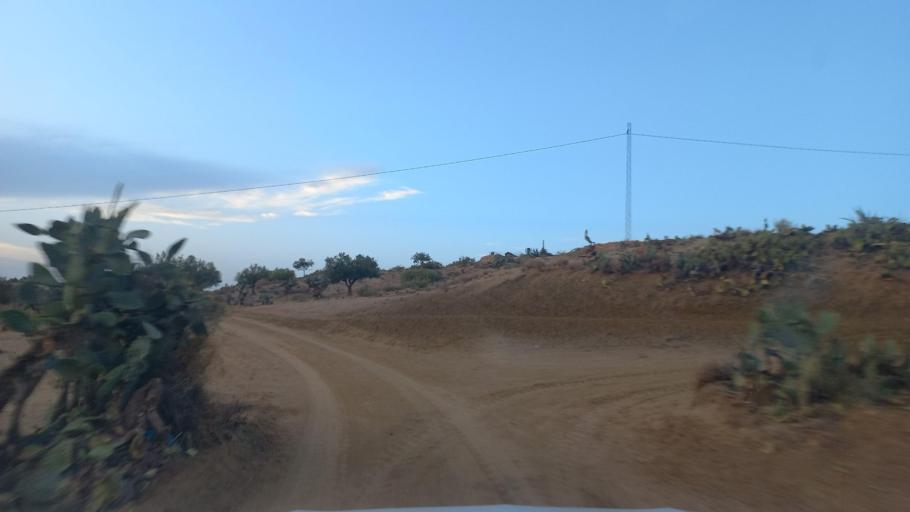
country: TN
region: Al Qasrayn
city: Kasserine
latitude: 35.2079
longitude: 9.0530
